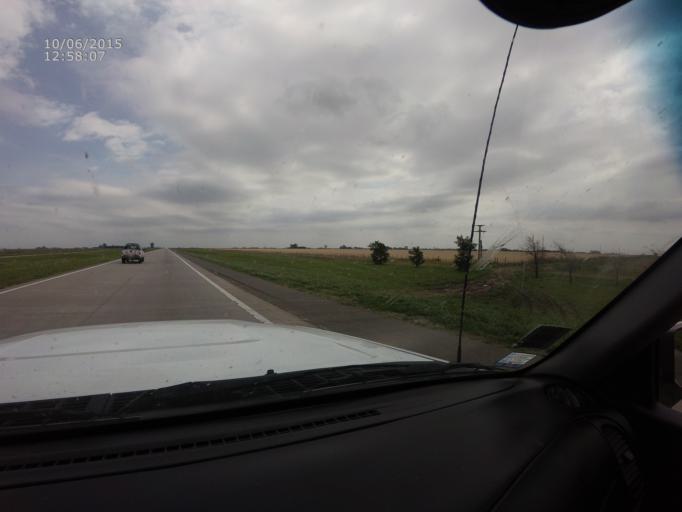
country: AR
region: Santa Fe
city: Armstrong
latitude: -32.8019
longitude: -61.6498
